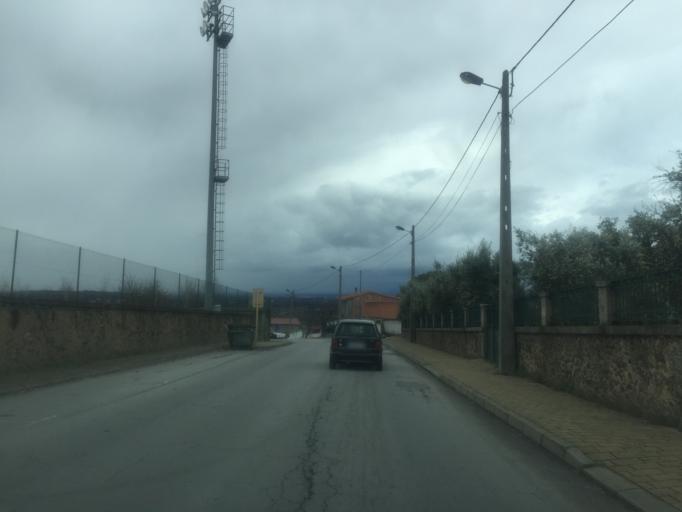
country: PT
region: Guarda
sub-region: Seia
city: Seia
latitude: 40.4042
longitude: -7.7182
